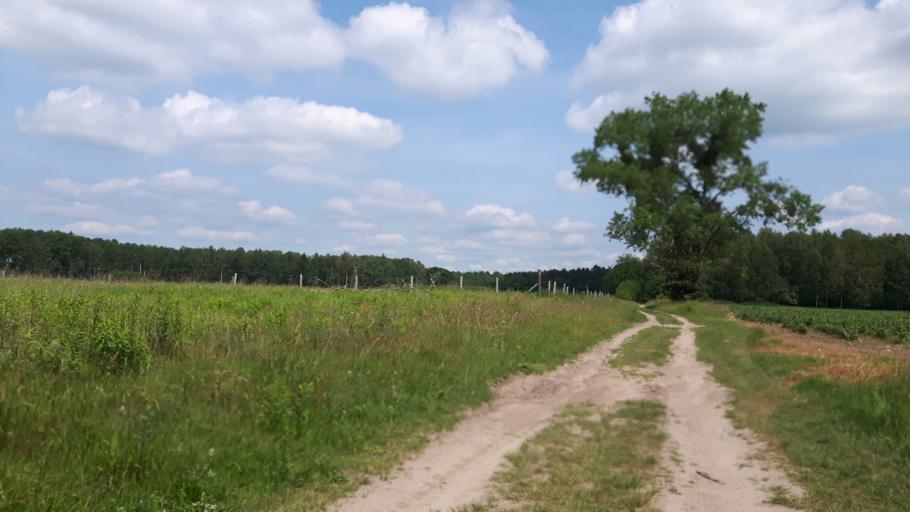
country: PL
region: West Pomeranian Voivodeship
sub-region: Powiat goleniowski
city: Goleniow
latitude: 53.6055
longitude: 14.8759
